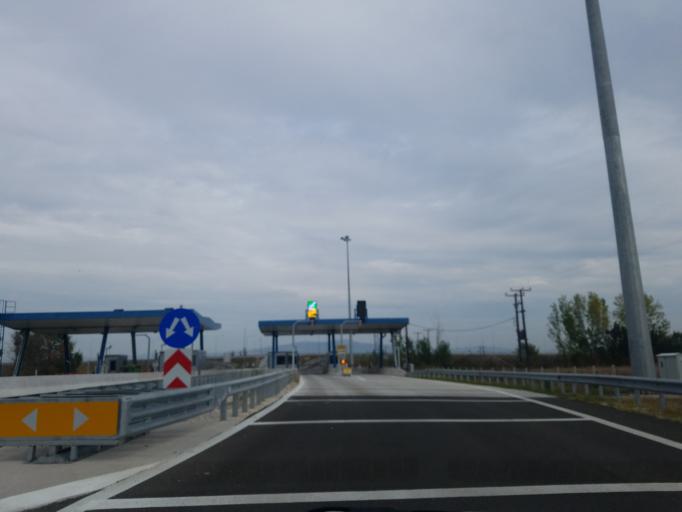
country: GR
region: Thessaly
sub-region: Nomos Kardhitsas
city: Agia Triada
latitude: 39.4740
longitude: 21.9032
